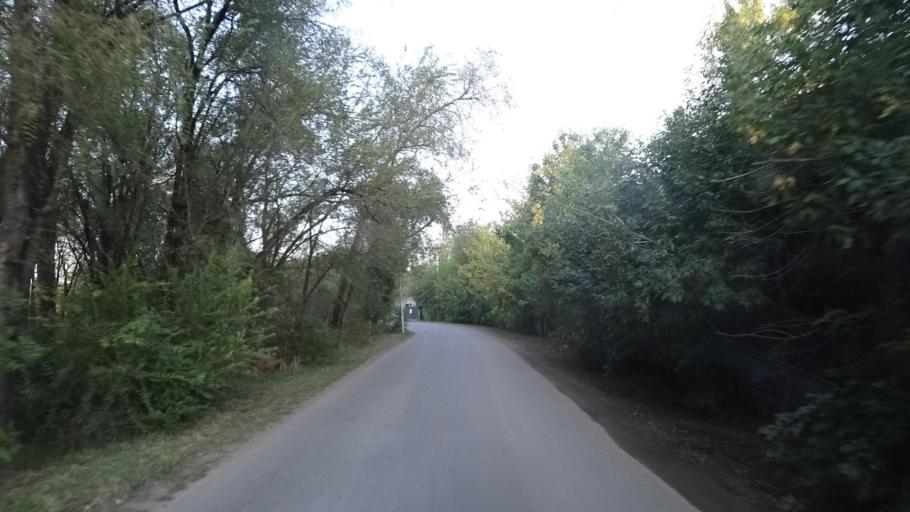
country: KZ
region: Almaty Oblysy
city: Pervomayskiy
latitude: 43.3296
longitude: 76.9991
